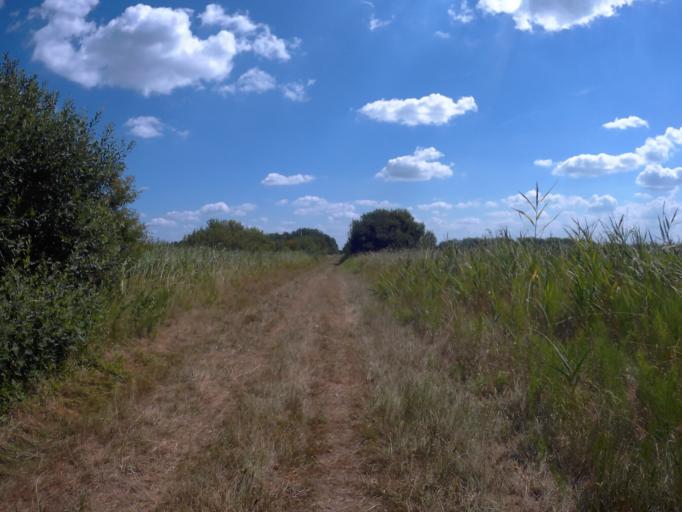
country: DE
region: Schleswig-Holstein
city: Hude
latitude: 54.3788
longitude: 9.2092
